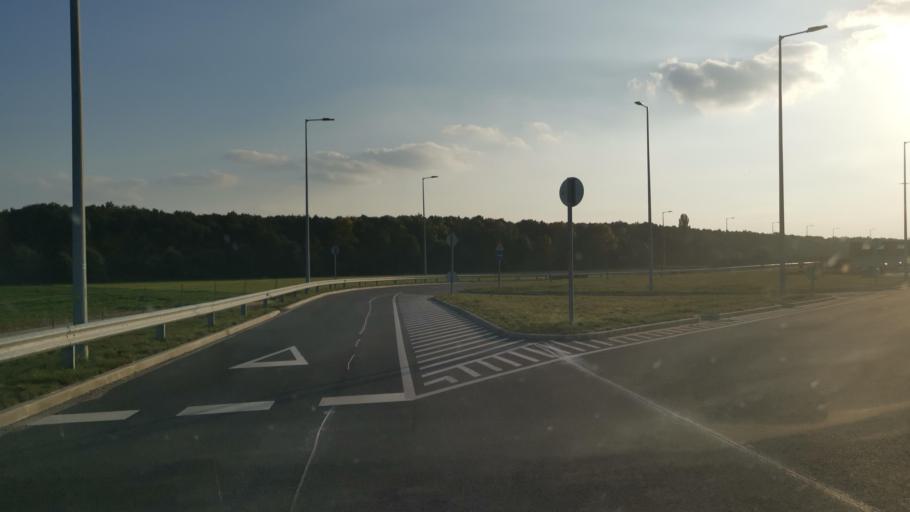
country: HU
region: Gyor-Moson-Sopron
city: Mihalyi
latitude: 47.5633
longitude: 17.0881
